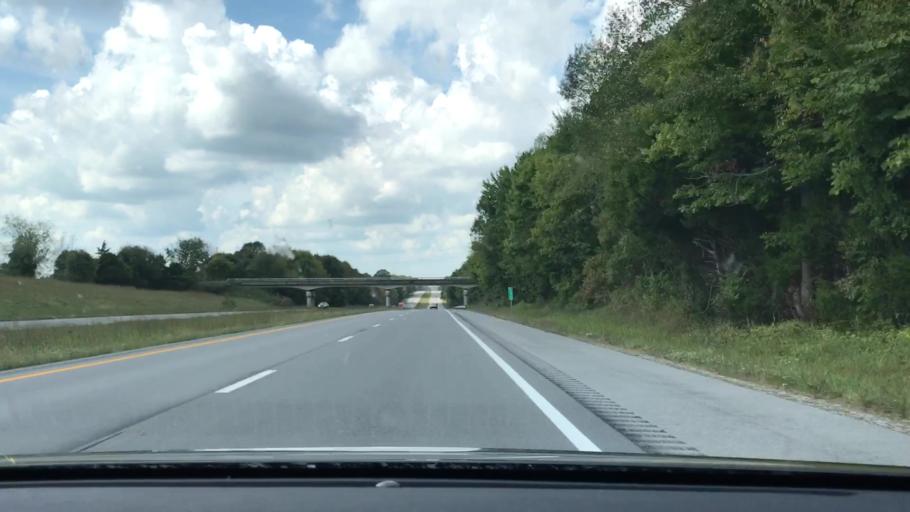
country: US
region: Kentucky
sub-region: Adair County
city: Columbia
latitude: 37.0710
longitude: -85.2149
